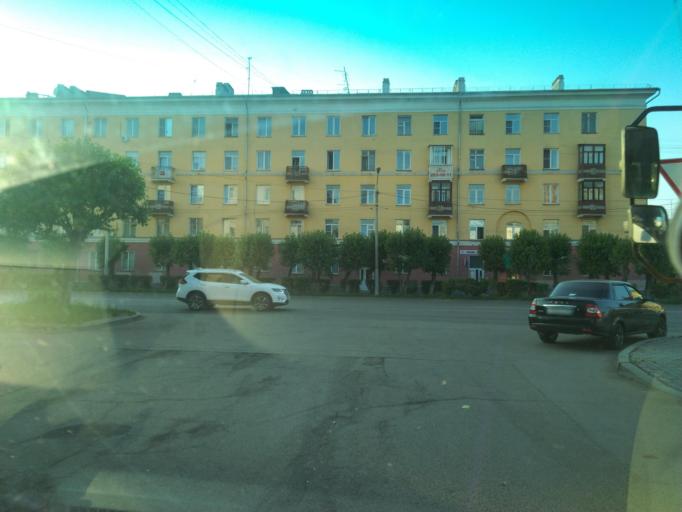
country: RU
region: Krasnoyarskiy
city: Krasnoyarsk
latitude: 55.9972
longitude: 92.9276
